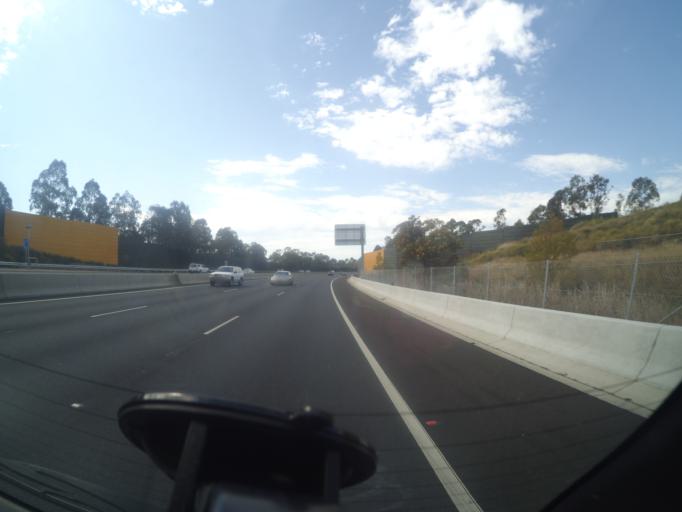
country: AU
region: New South Wales
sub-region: Liverpool
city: Miller
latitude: -33.9381
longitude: 150.9065
